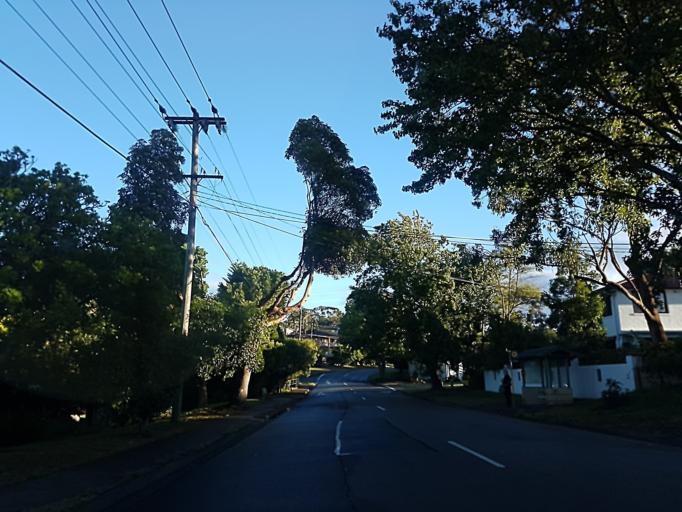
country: AU
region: New South Wales
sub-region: Warringah
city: Davidson
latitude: -33.7327
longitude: 151.2138
